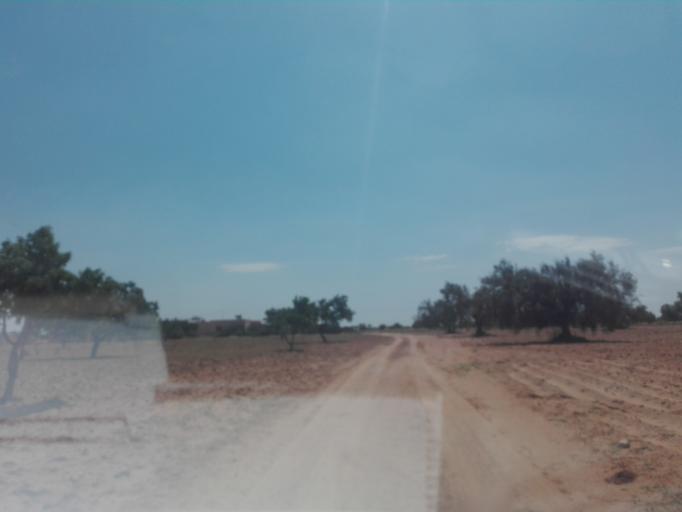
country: TN
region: Safaqis
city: Bi'r `Ali Bin Khalifah
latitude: 34.6125
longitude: 10.3508
